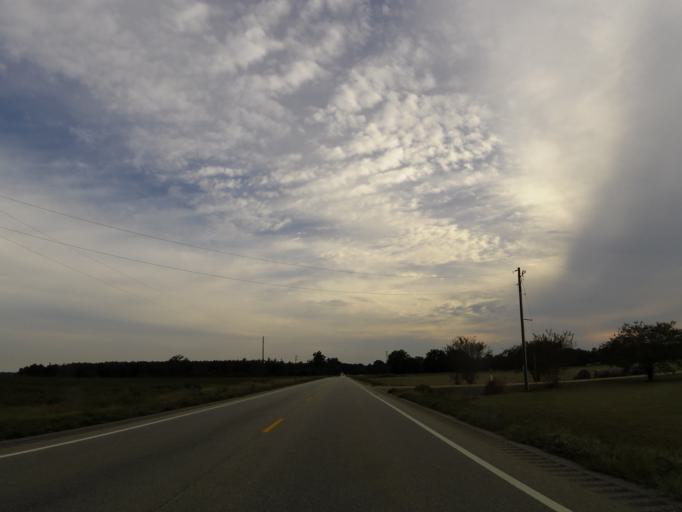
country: US
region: Alabama
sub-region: Monroe County
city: Frisco City
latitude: 31.3687
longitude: -87.4315
